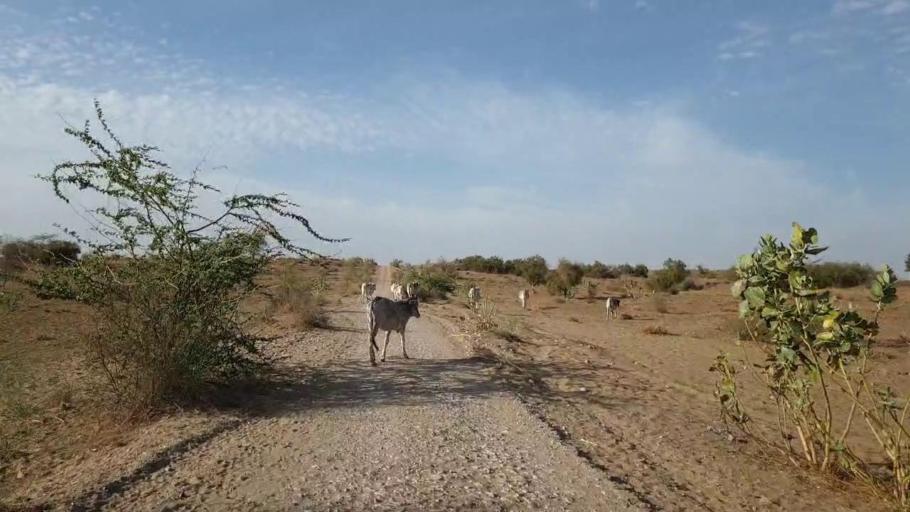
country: PK
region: Sindh
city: Nabisar
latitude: 25.0104
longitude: 69.9203
